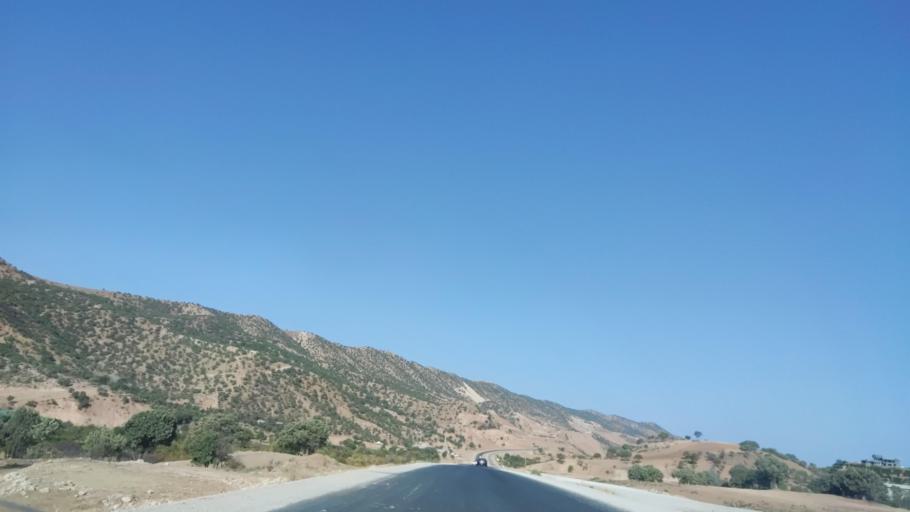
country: IQ
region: Arbil
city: Shaqlawah
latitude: 36.4302
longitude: 44.3253
